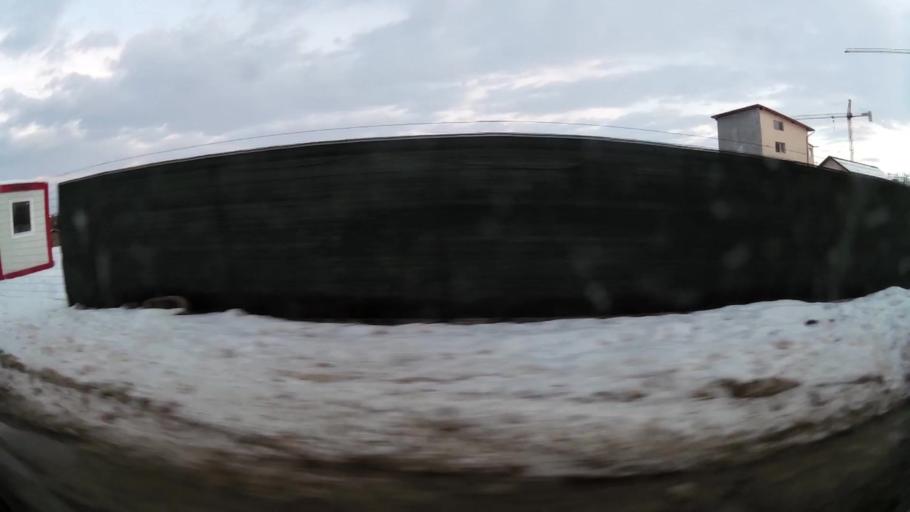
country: RO
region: Ilfov
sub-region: Comuna Popesti-Leordeni
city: Popesti-Leordeni
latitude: 44.3688
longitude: 26.1554
